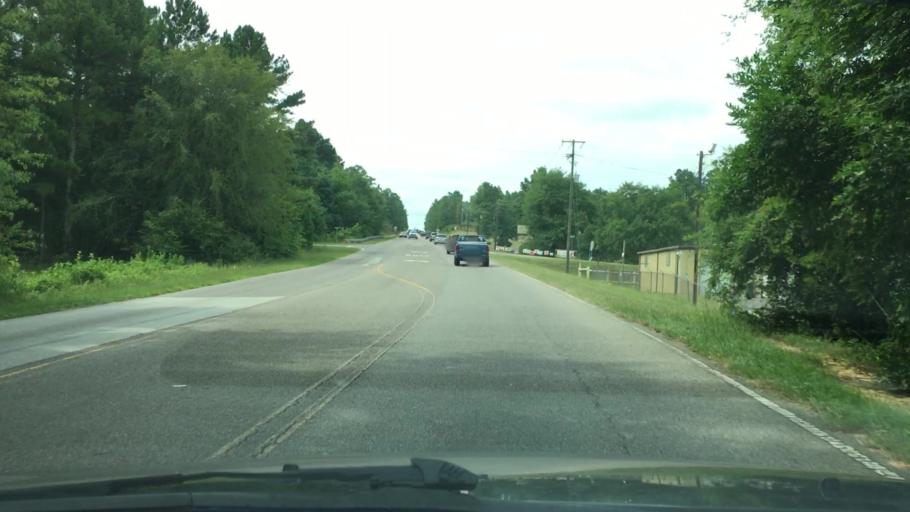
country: US
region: South Carolina
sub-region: Aiken County
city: Warrenville
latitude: 33.5558
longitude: -81.7788
